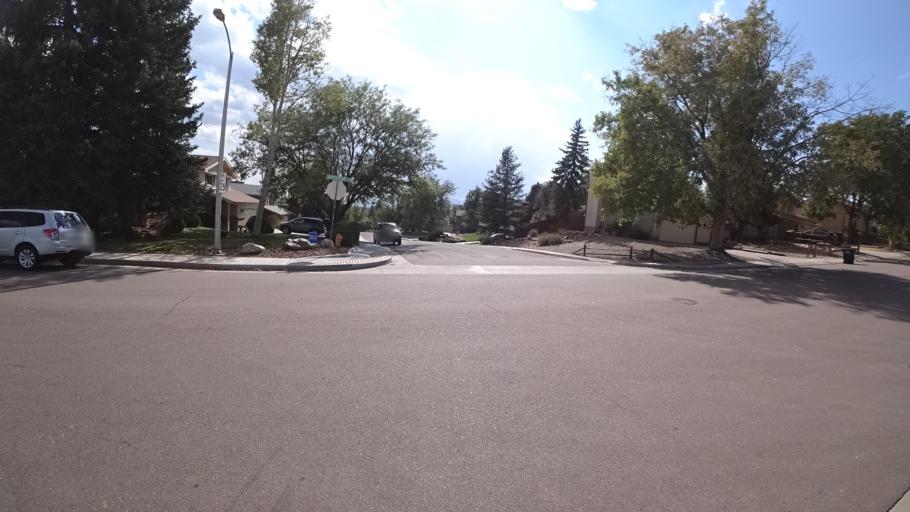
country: US
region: Colorado
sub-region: El Paso County
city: Cimarron Hills
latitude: 38.8725
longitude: -104.7296
